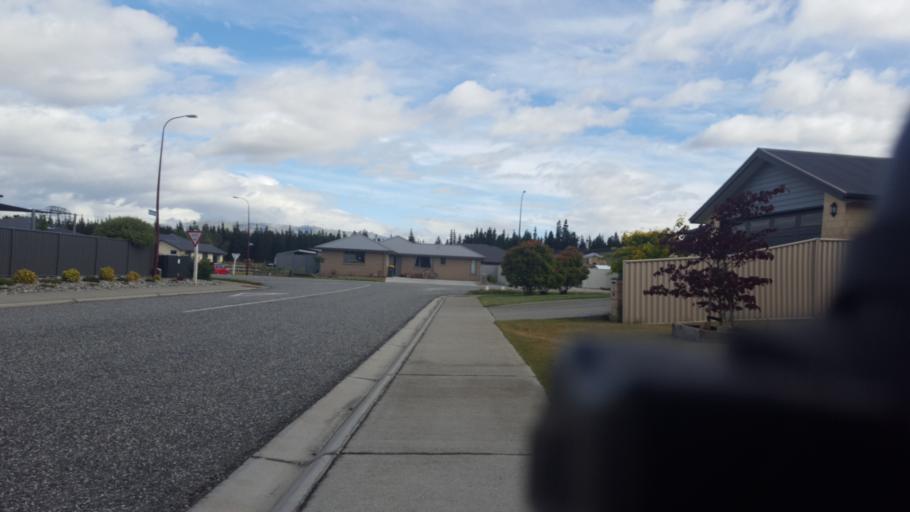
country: NZ
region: Otago
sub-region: Queenstown-Lakes District
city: Wanaka
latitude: -45.2393
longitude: 169.3818
